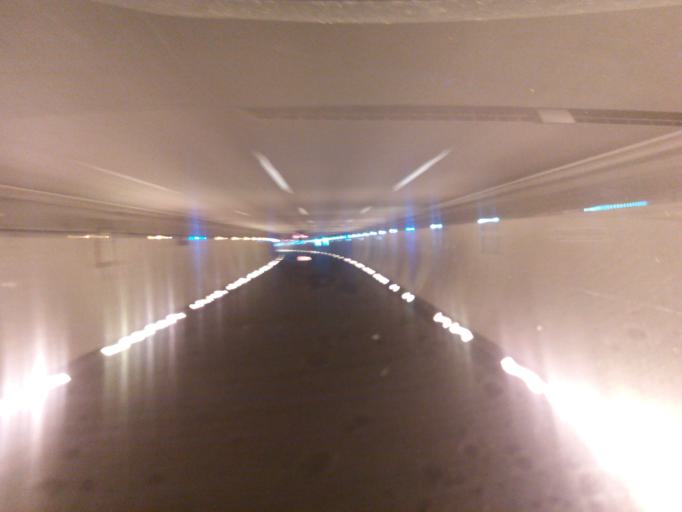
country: ES
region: Madrid
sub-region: Provincia de Madrid
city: Fuencarral-El Pardo
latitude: 40.4841
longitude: -3.7436
